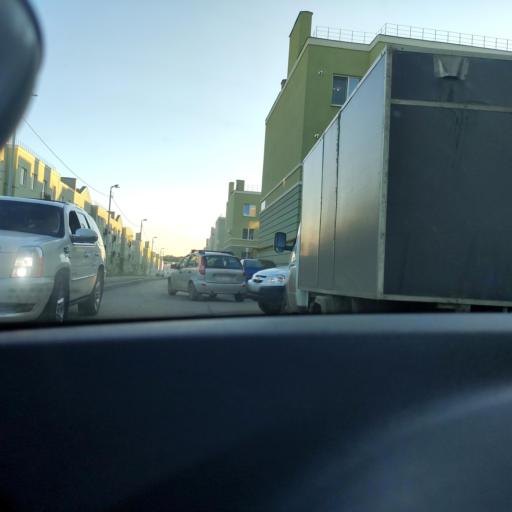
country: RU
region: Samara
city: Petra-Dubrava
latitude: 53.3126
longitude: 50.3127
